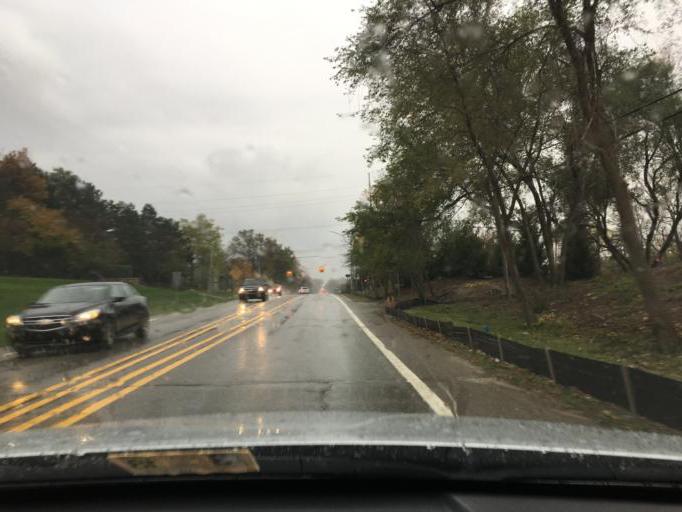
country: US
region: Michigan
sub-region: Oakland County
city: Auburn Hills
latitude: 42.7114
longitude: -83.1956
